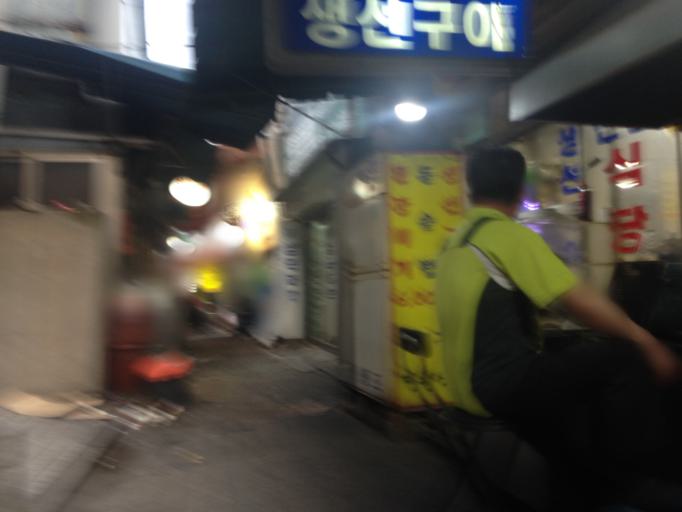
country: KR
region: Seoul
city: Seoul
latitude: 37.5701
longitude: 126.9931
